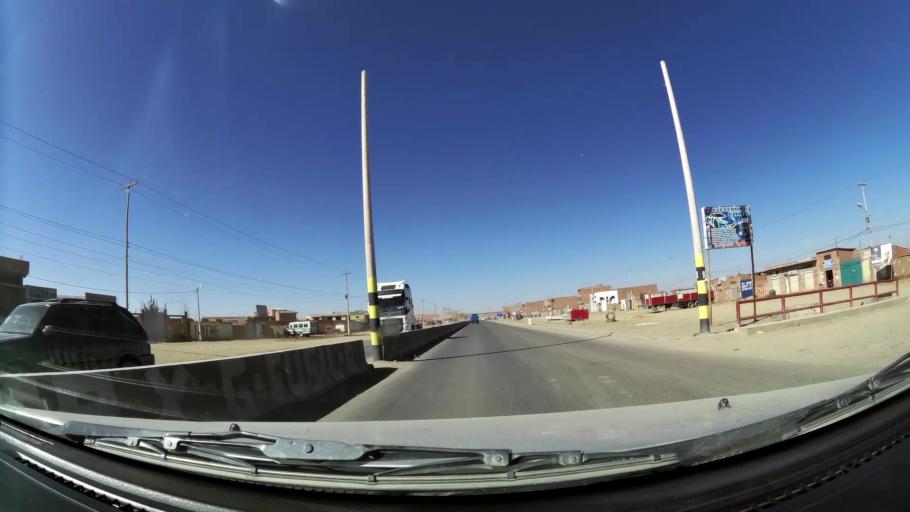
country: BO
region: La Paz
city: La Paz
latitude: -16.6088
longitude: -68.1832
